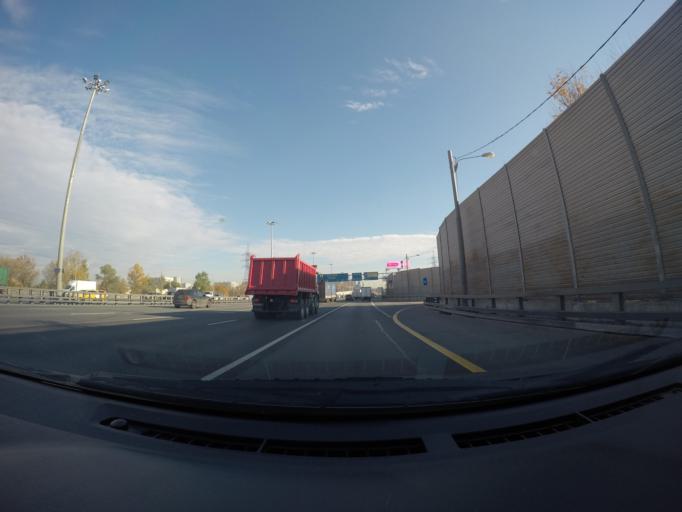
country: RU
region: Moskovskaya
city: Druzhba
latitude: 55.9064
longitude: 37.7648
